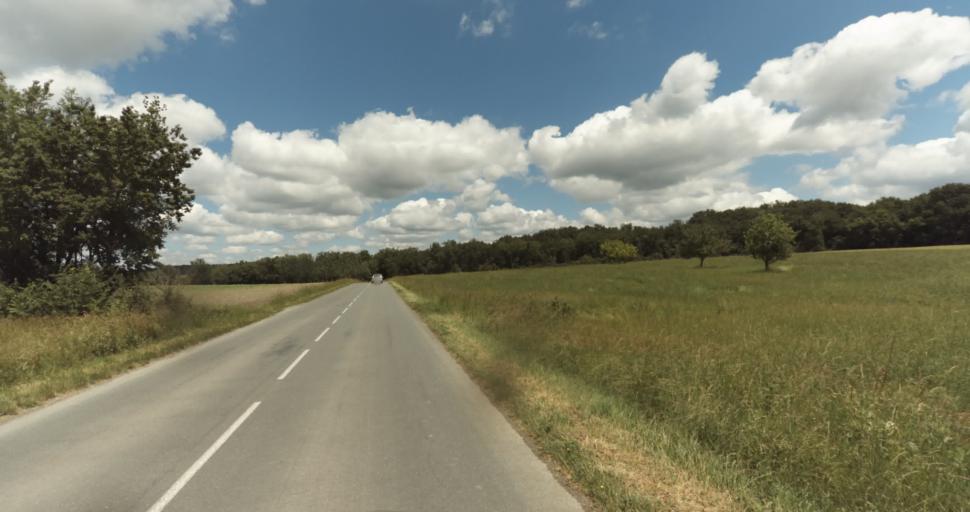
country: FR
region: Aquitaine
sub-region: Departement de la Dordogne
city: Beaumont-du-Perigord
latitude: 44.7091
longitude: 0.7501
